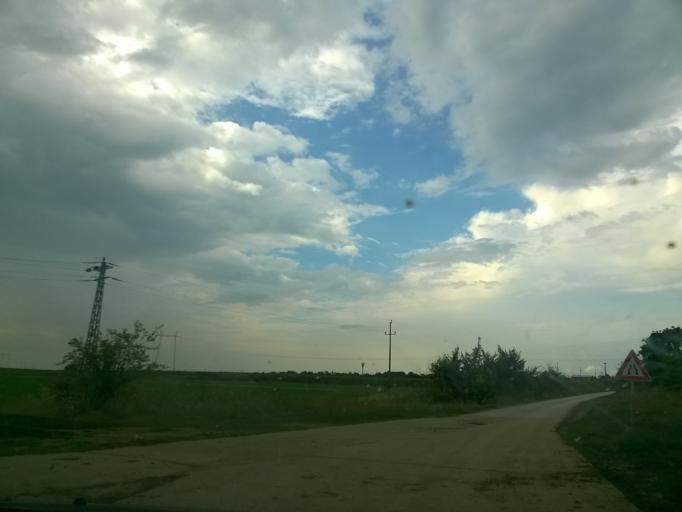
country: RS
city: Tomasevac
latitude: 45.2835
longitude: 20.6355
